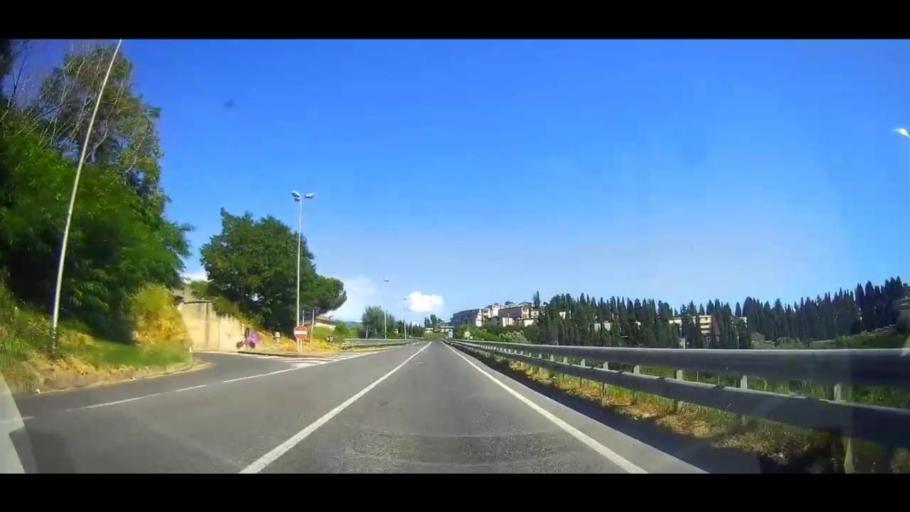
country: IT
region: Calabria
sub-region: Provincia di Cosenza
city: Cosenza
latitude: 39.2948
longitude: 16.2656
